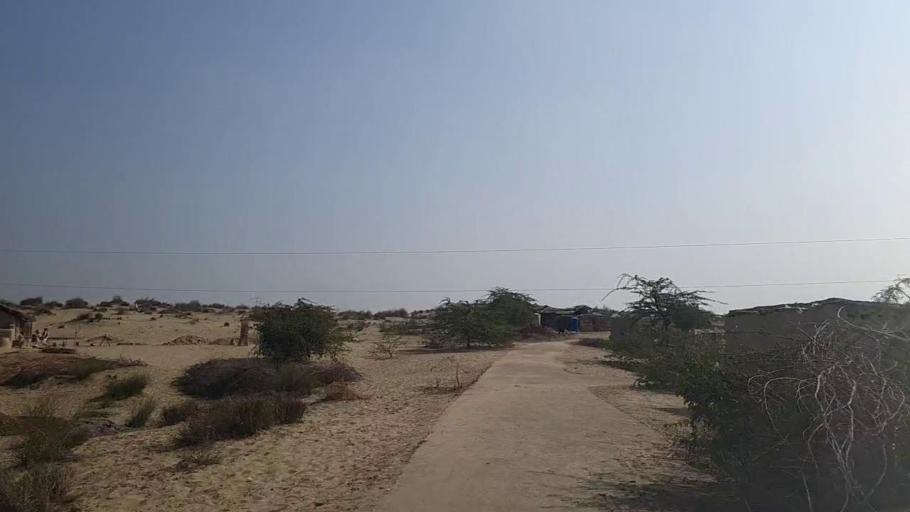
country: PK
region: Sindh
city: Daur
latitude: 26.4657
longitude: 68.4575
